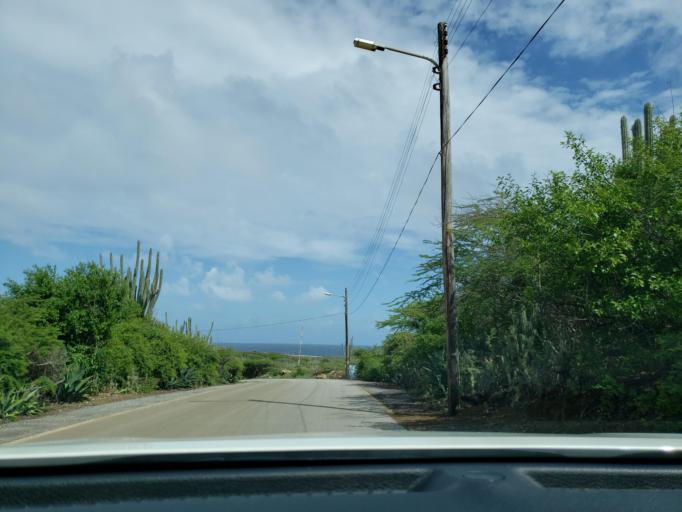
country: CW
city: Barber
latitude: 12.3653
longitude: -69.1166
